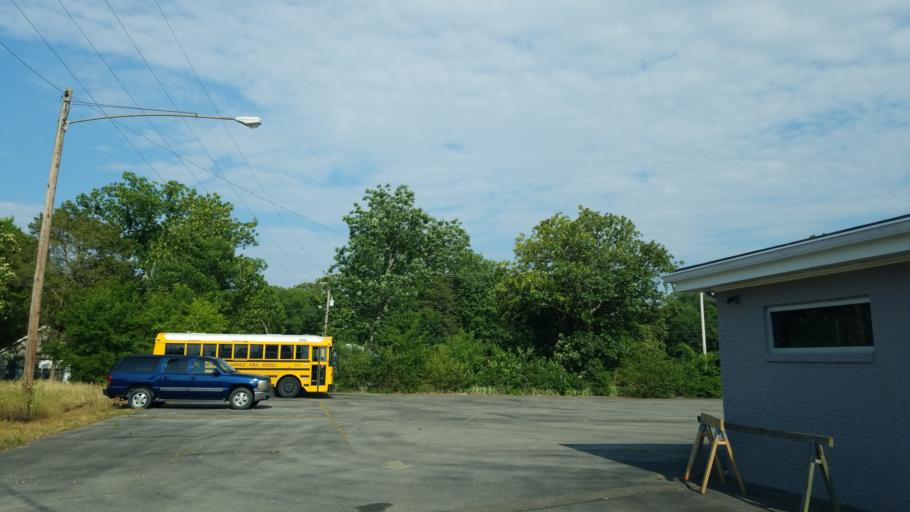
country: US
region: Tennessee
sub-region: Rutherford County
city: La Vergne
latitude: 36.0469
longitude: -86.5829
